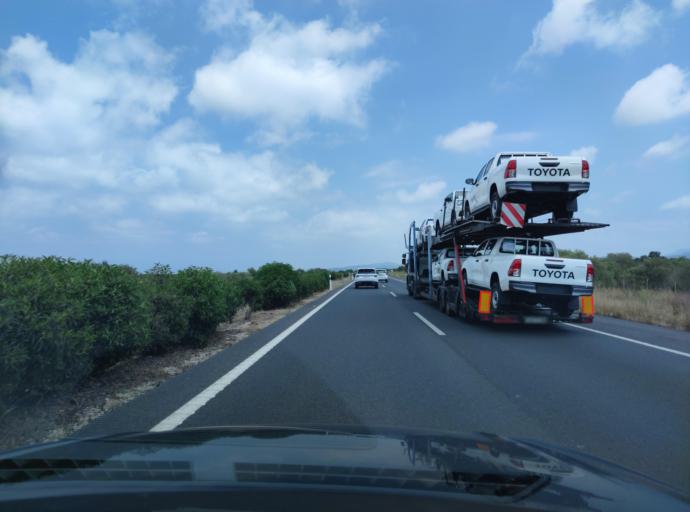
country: ES
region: Catalonia
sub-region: Provincia de Tarragona
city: Alcanar
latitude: 40.5155
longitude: 0.4156
